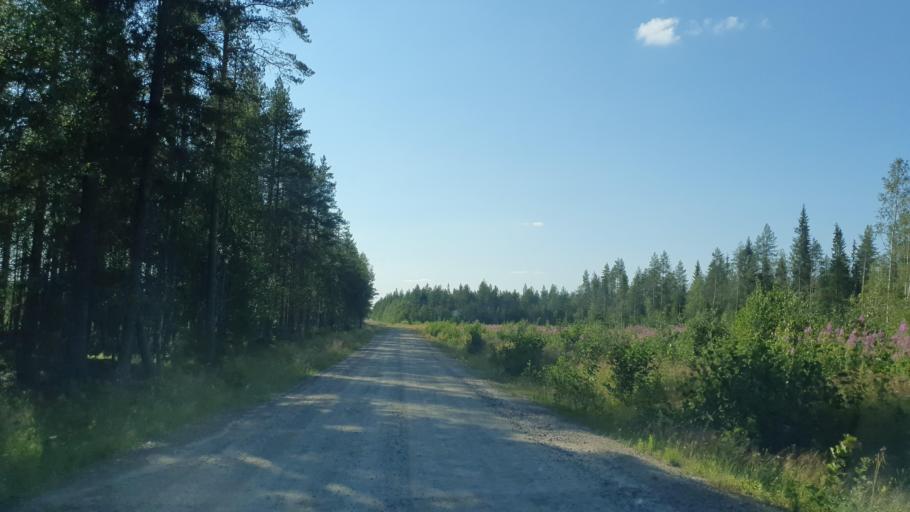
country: FI
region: Kainuu
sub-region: Kehys-Kainuu
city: Kuhmo
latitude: 64.0188
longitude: 29.7471
